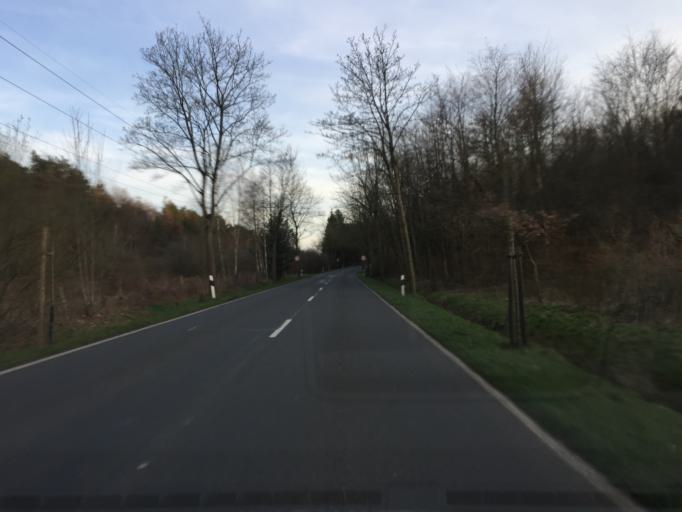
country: DE
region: Lower Saxony
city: Neustadt am Rubenberge
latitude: 52.4935
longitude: 9.4884
